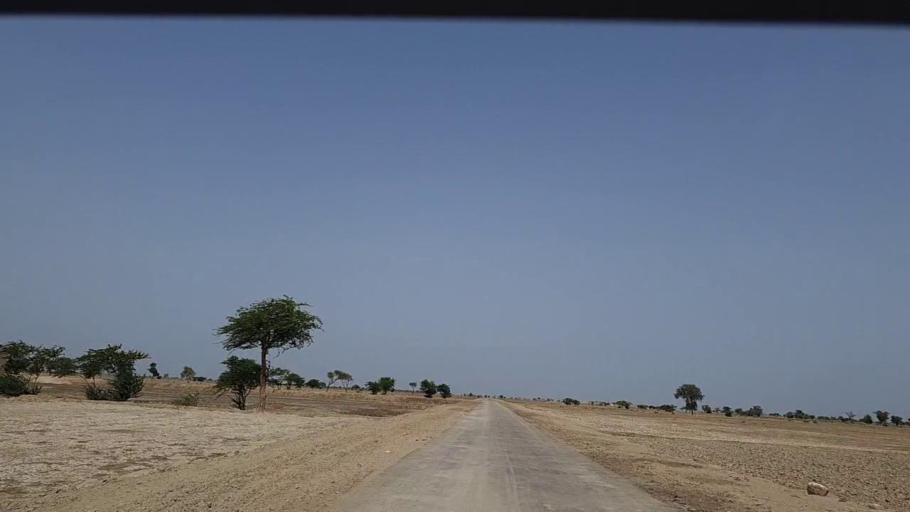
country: PK
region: Sindh
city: Johi
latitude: 26.7706
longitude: 67.6338
